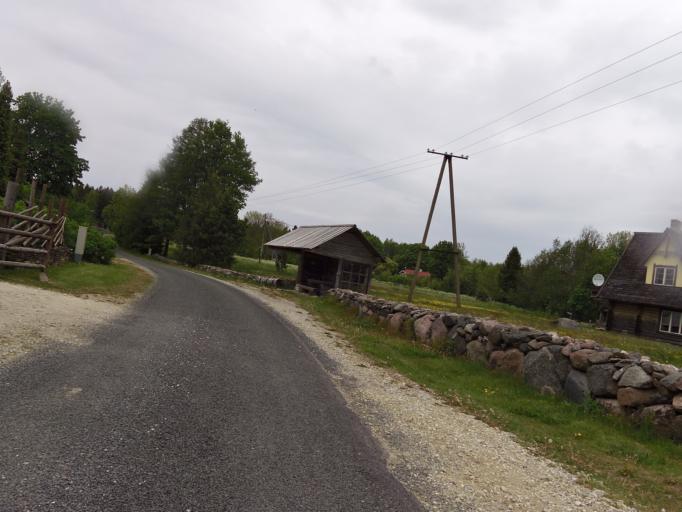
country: EE
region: Harju
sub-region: Paldiski linn
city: Paldiski
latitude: 59.2557
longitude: 23.7482
